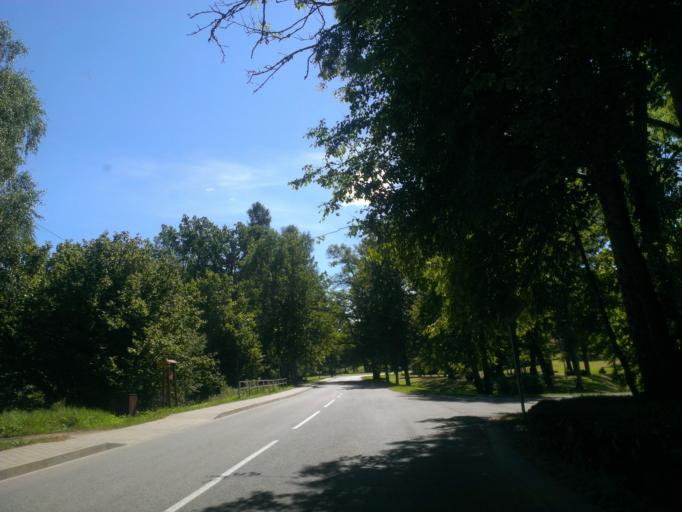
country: LV
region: Malpils
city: Malpils
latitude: 57.0095
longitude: 24.9502
